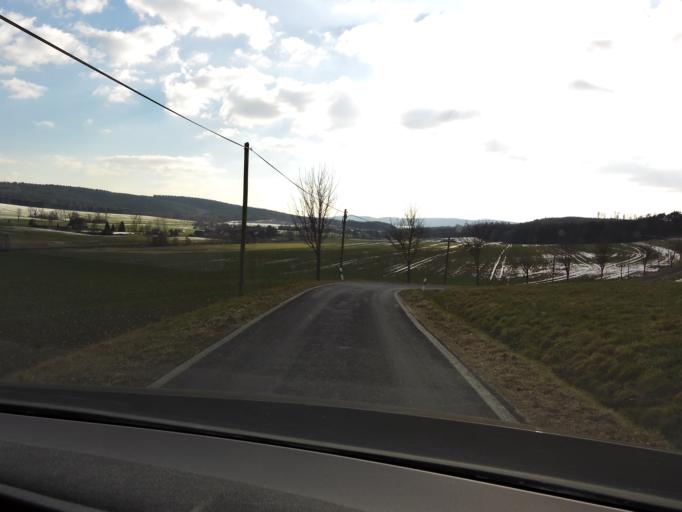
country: DE
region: Thuringia
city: Leimbach
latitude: 50.8573
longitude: 10.2175
